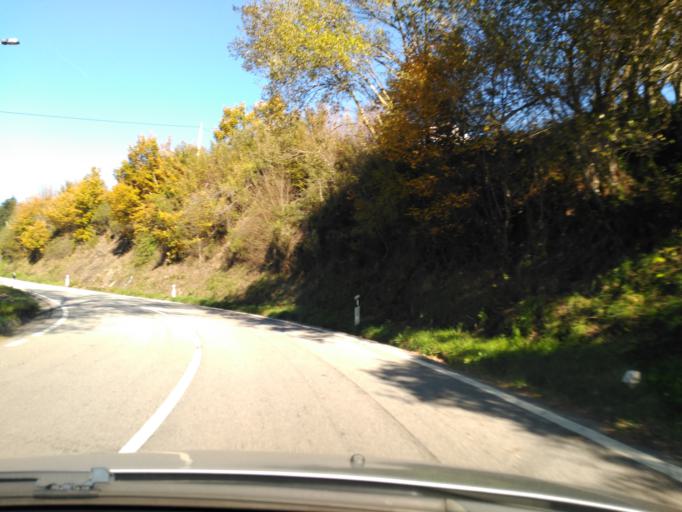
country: PT
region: Braga
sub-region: Cabeceiras de Basto
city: Cabeceiras de Basto
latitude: 41.6718
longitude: -7.9606
